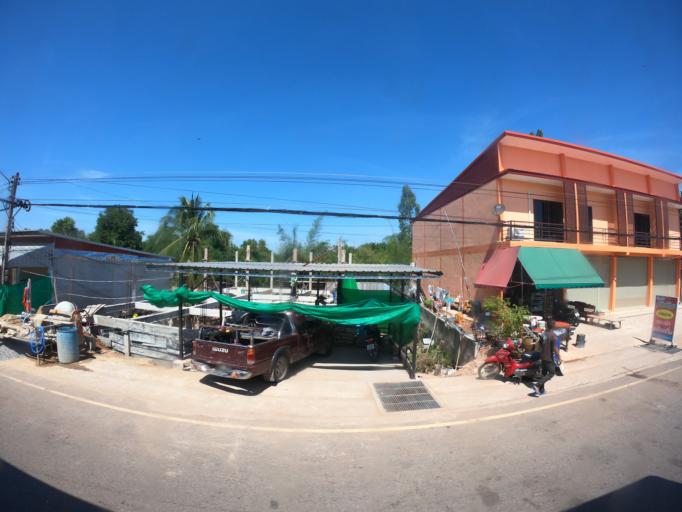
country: TH
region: Khon Kaen
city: Ban Phai
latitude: 16.0572
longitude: 102.7203
